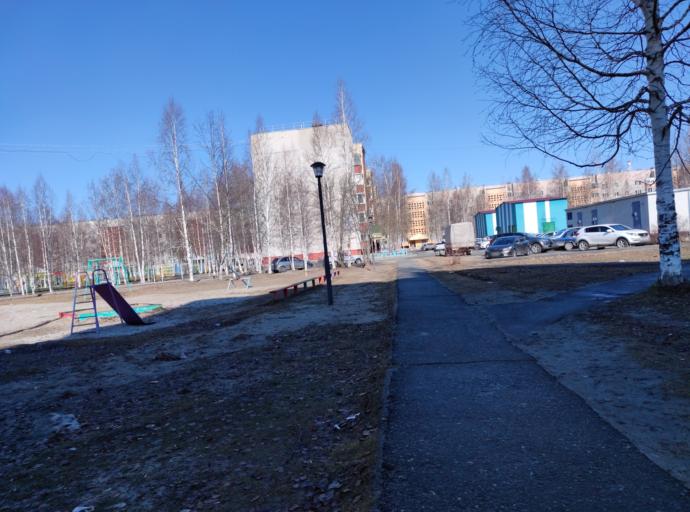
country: RU
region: Khanty-Mansiyskiy Avtonomnyy Okrug
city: Langepas
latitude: 61.2502
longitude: 75.1777
